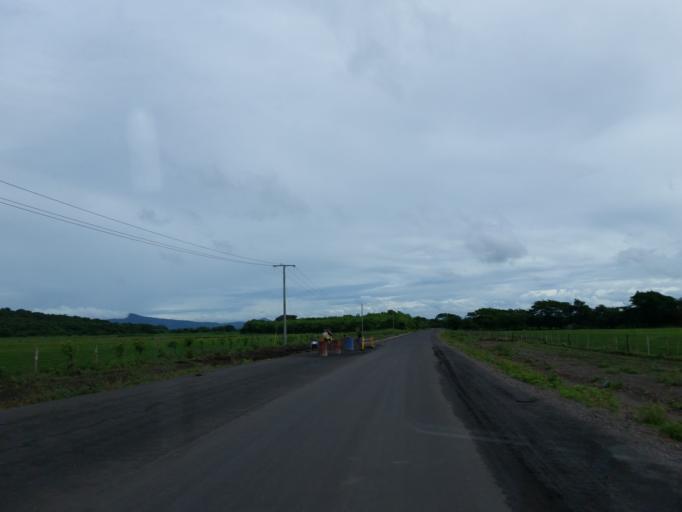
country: NI
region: Leon
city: Larreynaga
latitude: 12.5170
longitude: -86.6025
